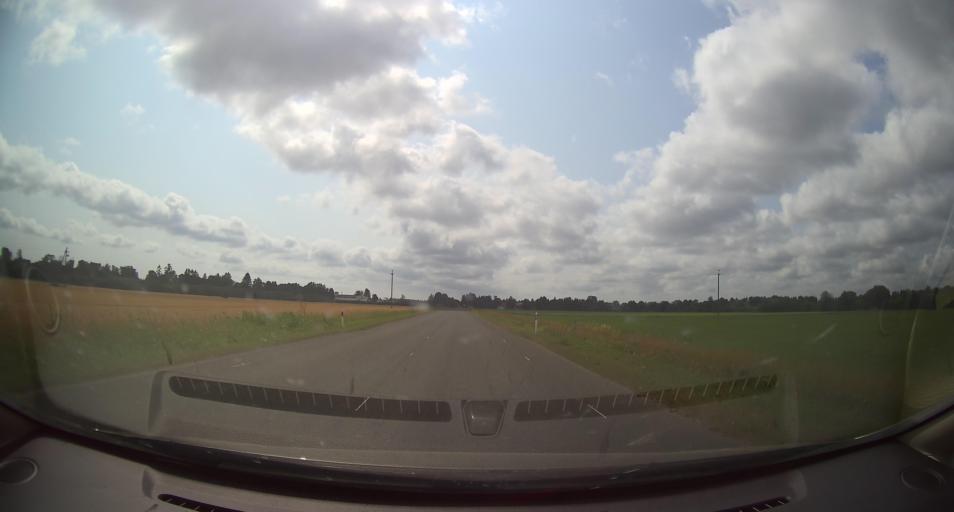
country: EE
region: Paernumaa
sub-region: Audru vald
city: Audru
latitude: 58.4811
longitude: 24.3327
